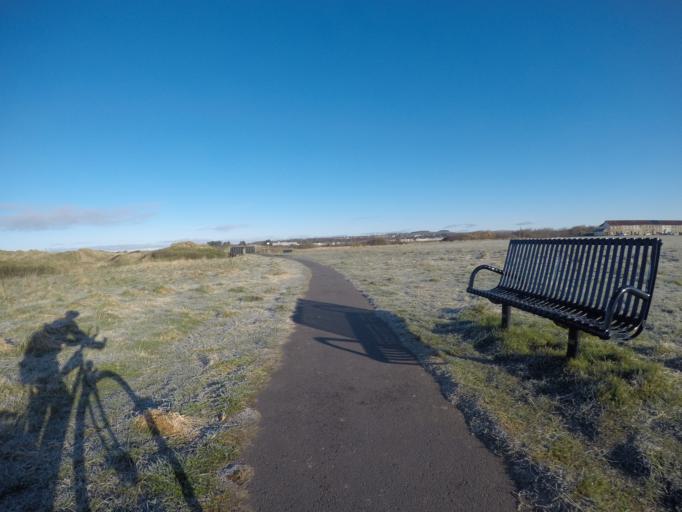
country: GB
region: Scotland
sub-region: North Ayrshire
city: Stevenston
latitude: 55.6309
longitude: -4.7556
